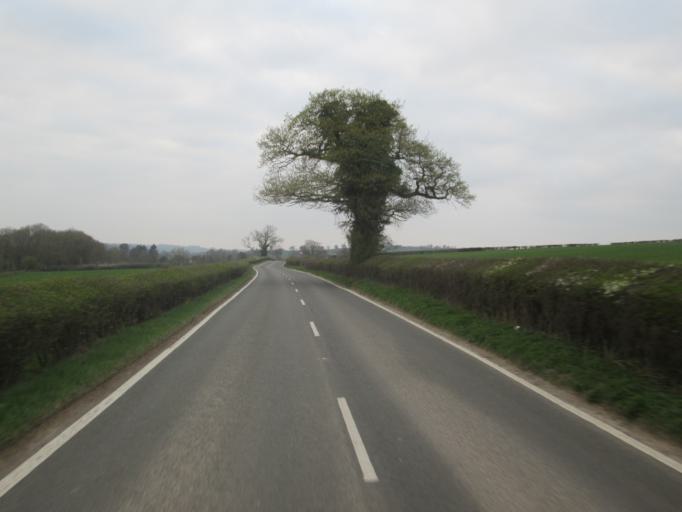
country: GB
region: England
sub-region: Derbyshire
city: Duffield
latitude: 53.0136
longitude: -1.5383
